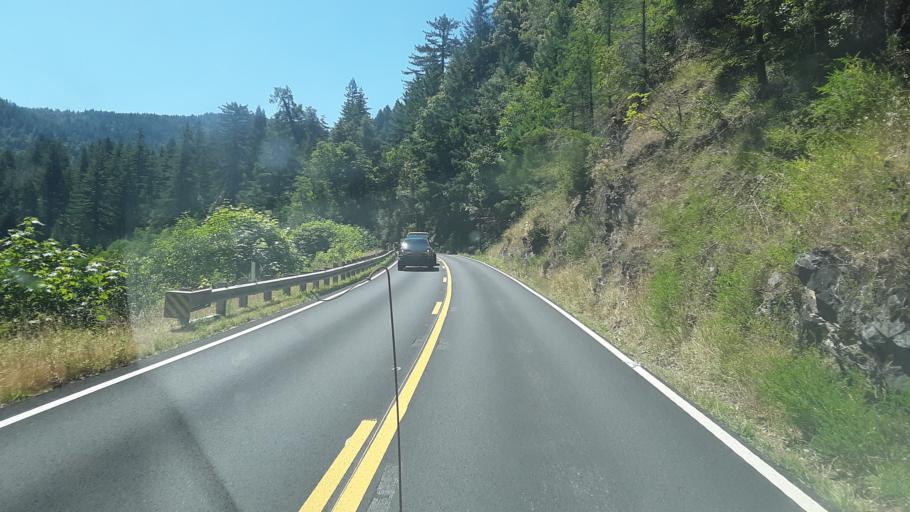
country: US
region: California
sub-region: Del Norte County
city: Bertsch-Oceanview
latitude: 41.8354
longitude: -124.0364
